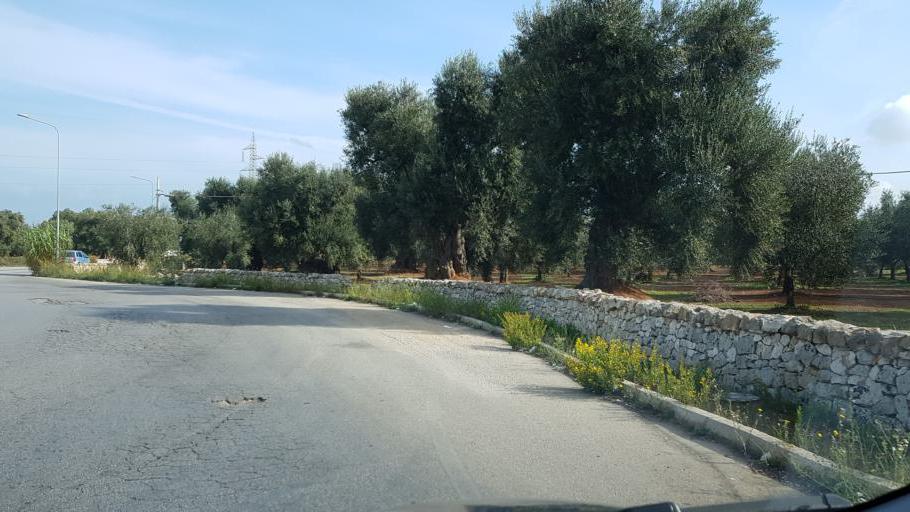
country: IT
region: Apulia
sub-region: Provincia di Brindisi
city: Ostuni
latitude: 40.7441
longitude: 17.5796
